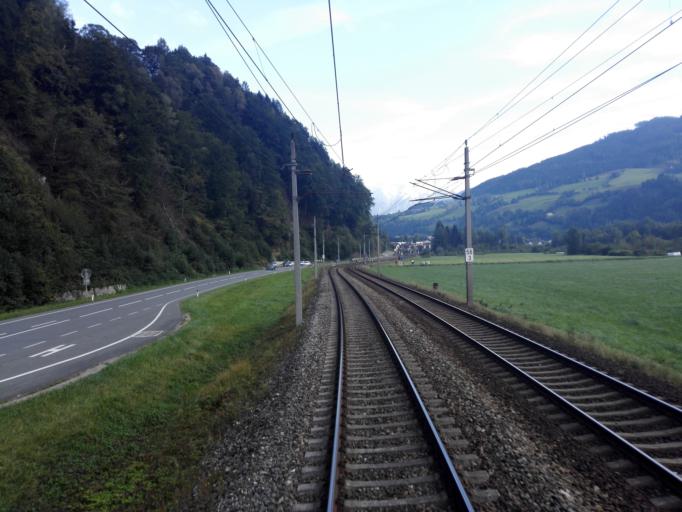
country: AT
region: Salzburg
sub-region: Politischer Bezirk Sankt Johann im Pongau
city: Bischofshofen
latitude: 47.3886
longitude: 13.2139
